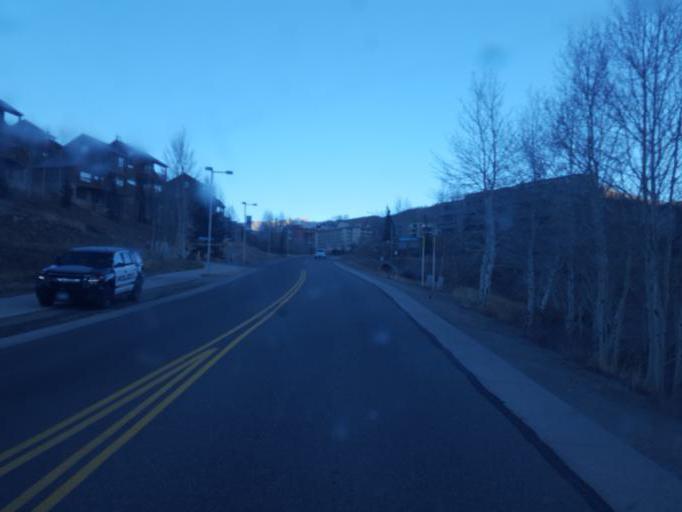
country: US
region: Colorado
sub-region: Gunnison County
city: Crested Butte
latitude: 38.8946
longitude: -106.9699
